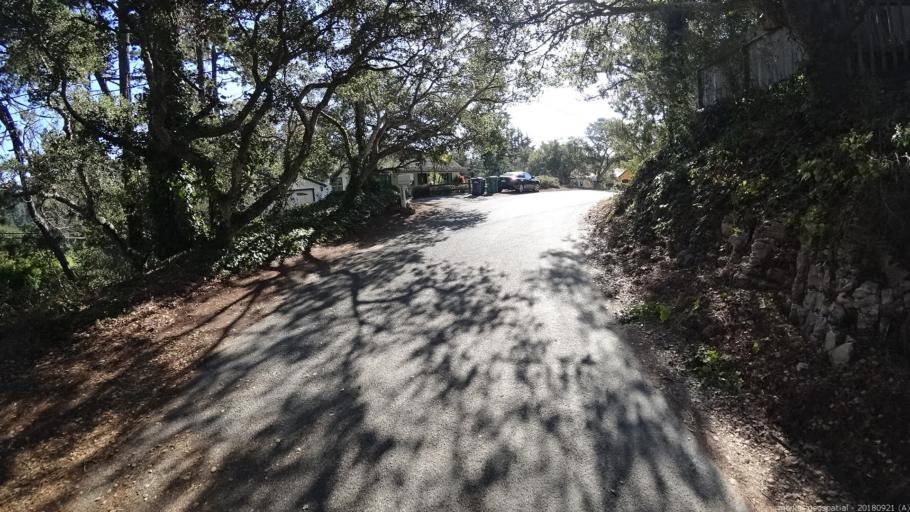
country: US
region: California
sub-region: Monterey County
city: Carmel-by-the-Sea
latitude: 36.5687
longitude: -121.9139
